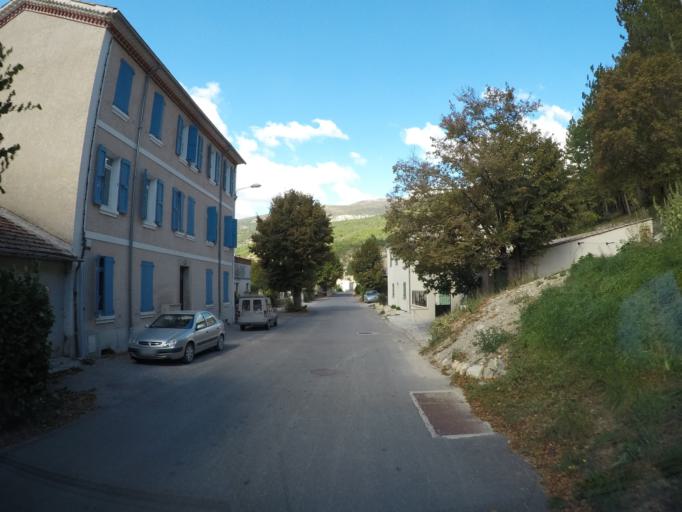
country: FR
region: Provence-Alpes-Cote d'Azur
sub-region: Departement des Hautes-Alpes
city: Laragne-Monteglin
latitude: 44.1691
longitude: 5.7438
